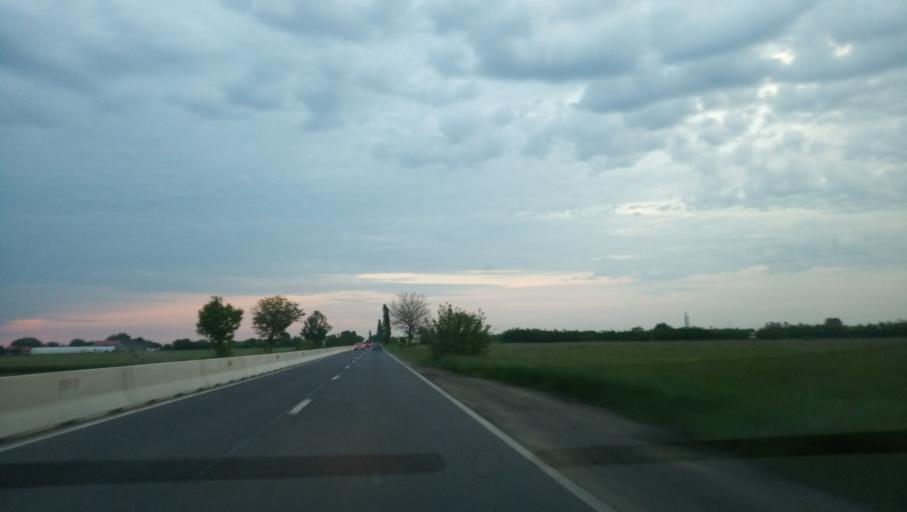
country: RO
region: Timis
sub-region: Comuna Sag
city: Sag
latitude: 45.6604
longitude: 21.1732
